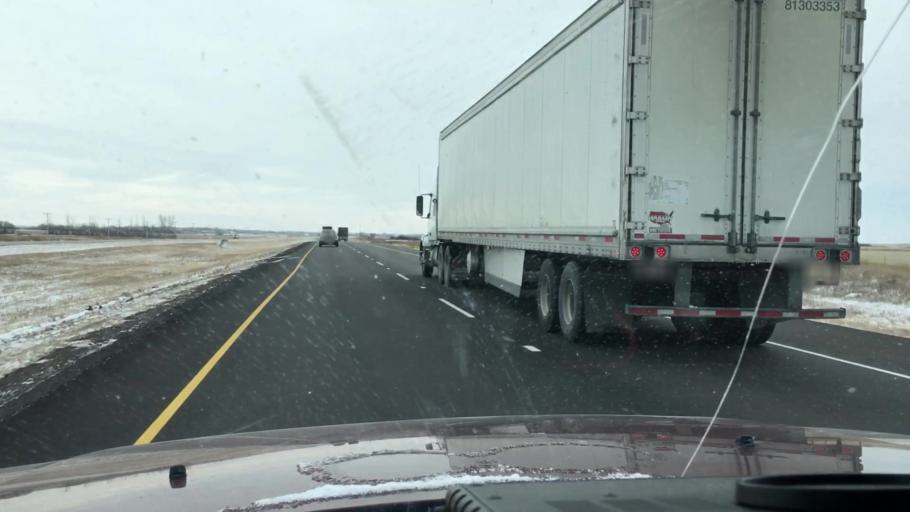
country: CA
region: Saskatchewan
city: Saskatoon
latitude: 51.7901
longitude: -106.4832
